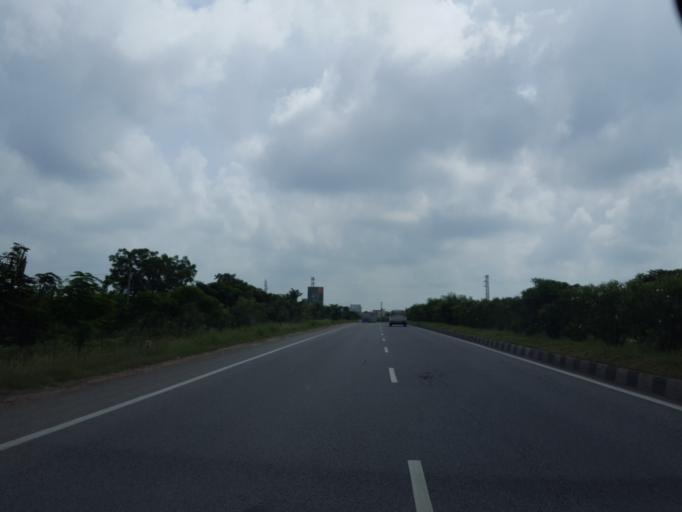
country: IN
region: Telangana
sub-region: Nalgonda
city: Nalgonda
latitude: 17.2298
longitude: 79.0151
